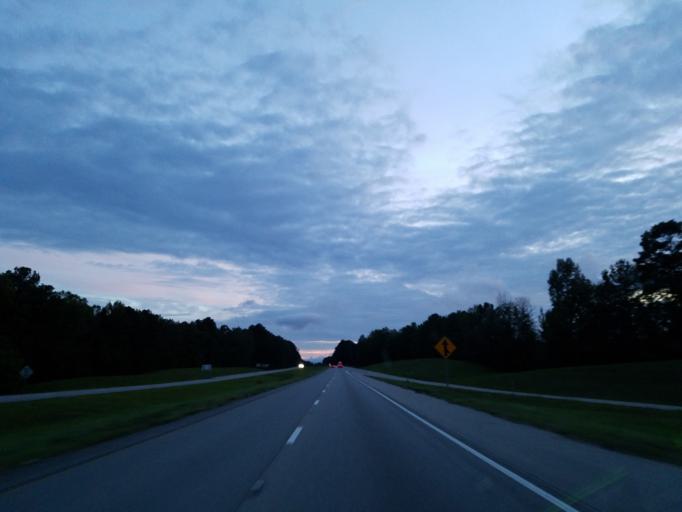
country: US
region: Mississippi
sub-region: Clarke County
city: Stonewall
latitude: 32.2037
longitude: -88.8450
